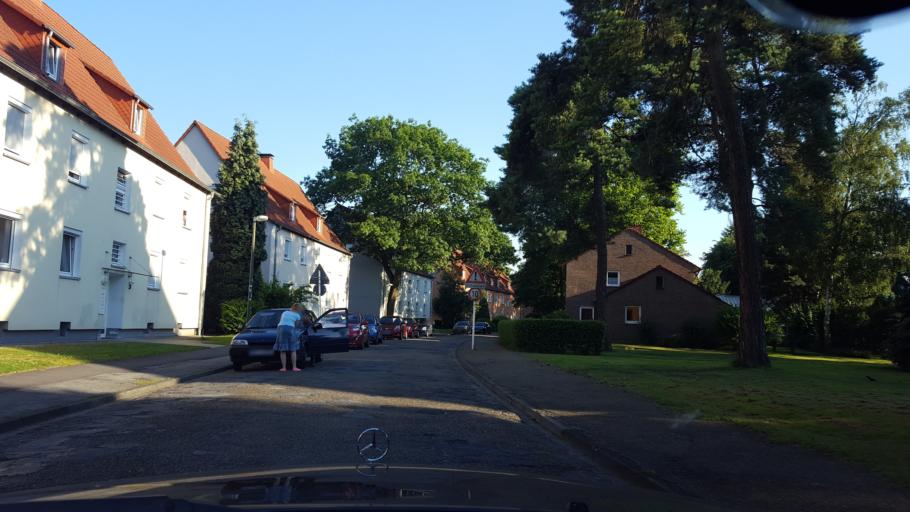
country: DE
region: North Rhine-Westphalia
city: Marl
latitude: 51.6659
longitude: 7.1029
